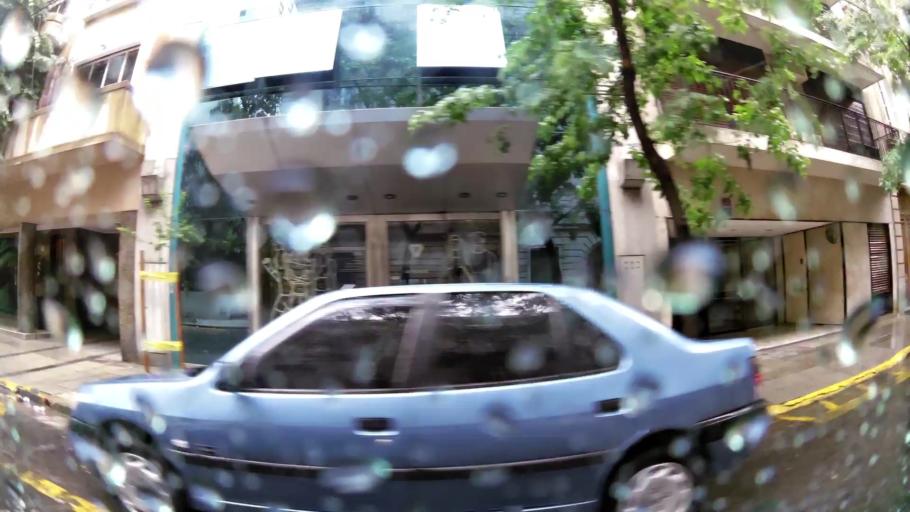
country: AR
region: Buenos Aires F.D.
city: Retiro
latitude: -34.5921
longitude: -58.3886
